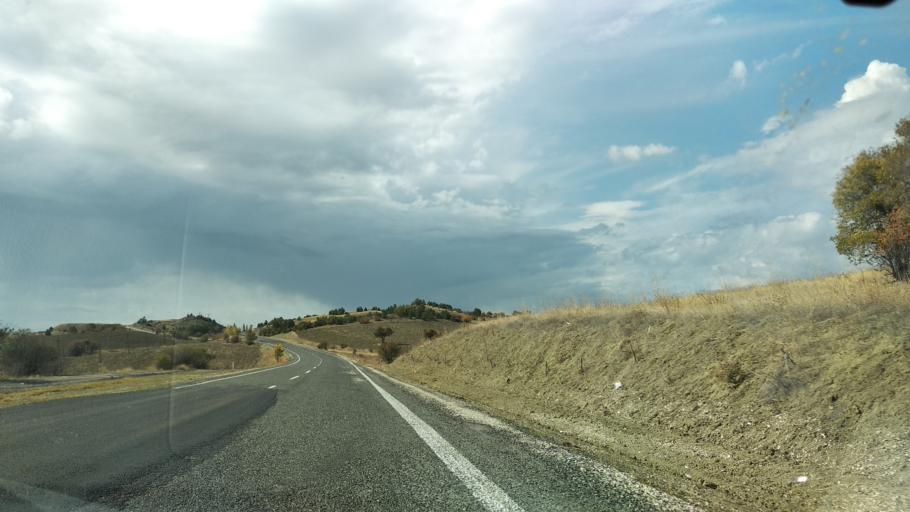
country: TR
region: Bolu
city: Seben
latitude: 40.3877
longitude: 31.5399
